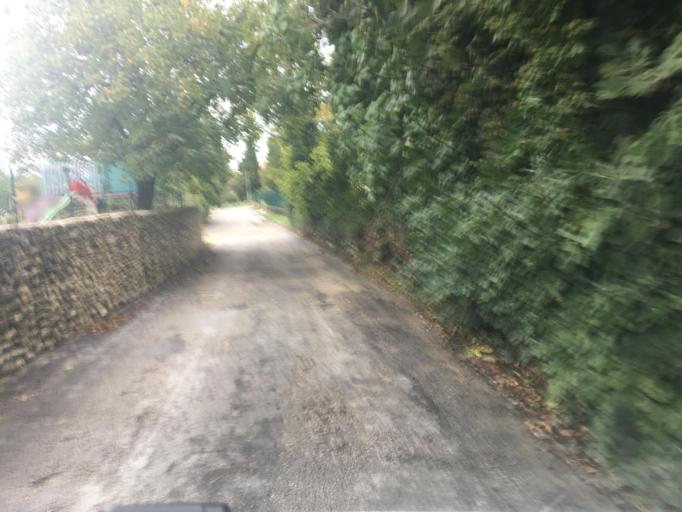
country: FR
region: Languedoc-Roussillon
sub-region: Departement du Gard
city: Uzes
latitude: 44.0173
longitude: 4.4116
